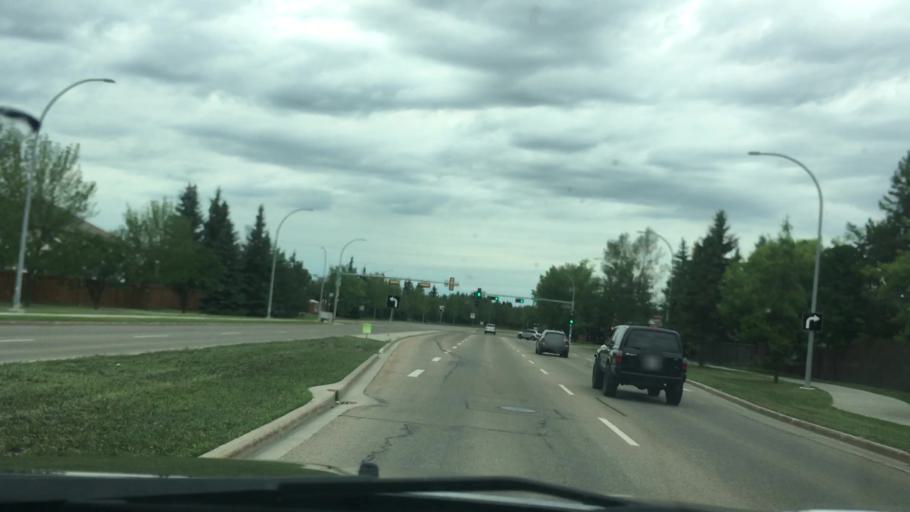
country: CA
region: Alberta
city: Edmonton
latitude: 53.4582
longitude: -113.5365
